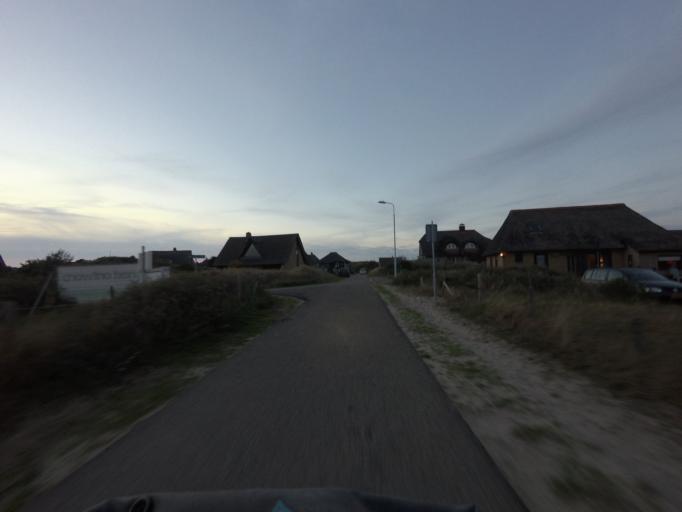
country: NL
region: Friesland
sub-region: Gemeente Ameland
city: Nes
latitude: 53.4572
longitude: 5.7957
